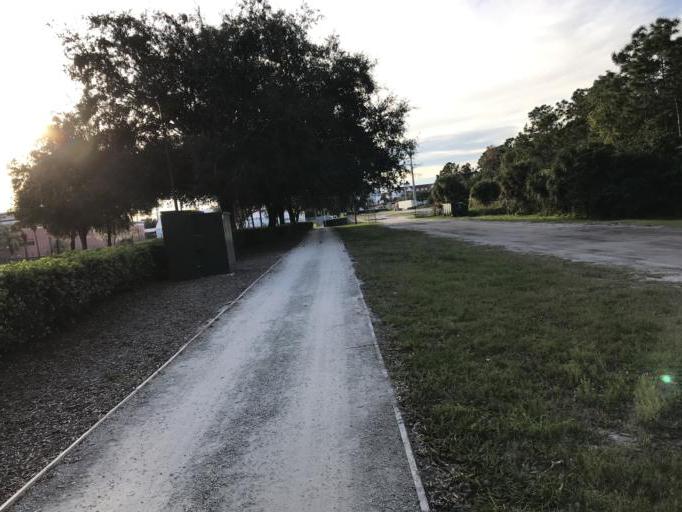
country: US
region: Florida
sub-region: Osceola County
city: Celebration
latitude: 28.3619
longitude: -81.4926
